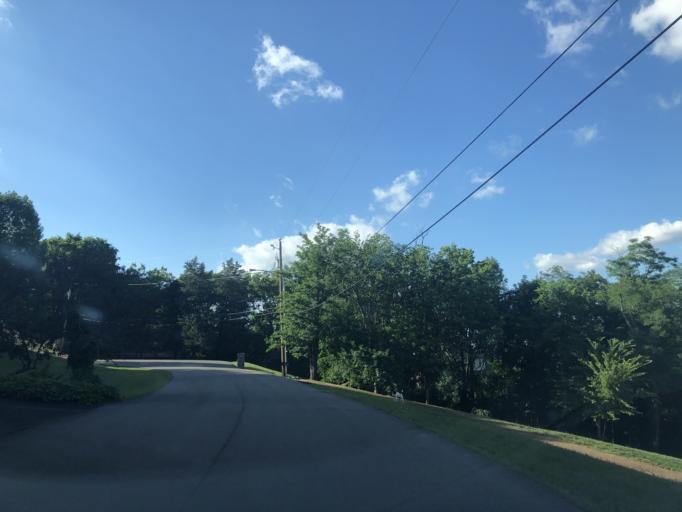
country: US
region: Tennessee
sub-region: Davidson County
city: Forest Hills
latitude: 36.0854
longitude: -86.8220
